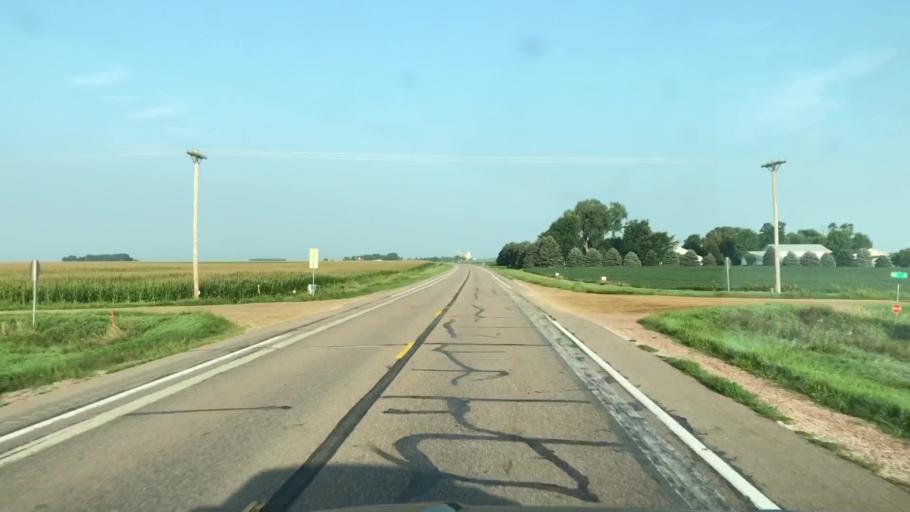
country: US
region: Iowa
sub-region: O'Brien County
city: Sheldon
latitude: 43.1856
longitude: -95.9605
